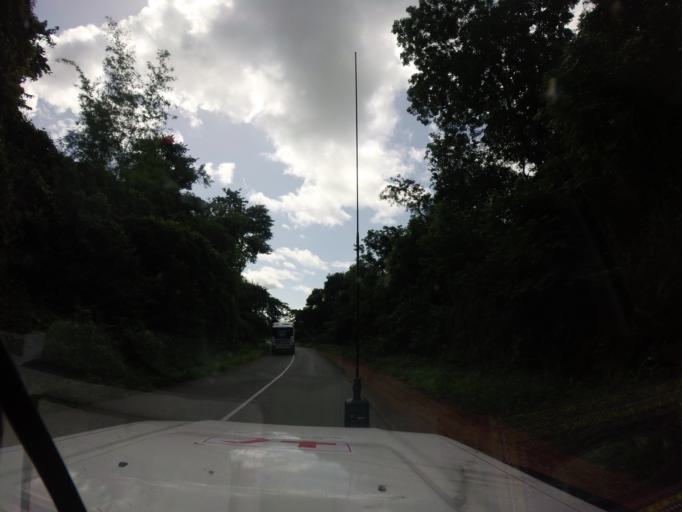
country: GN
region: Mamou
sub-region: Mamou Prefecture
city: Mamou
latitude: 10.2401
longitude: -11.8761
